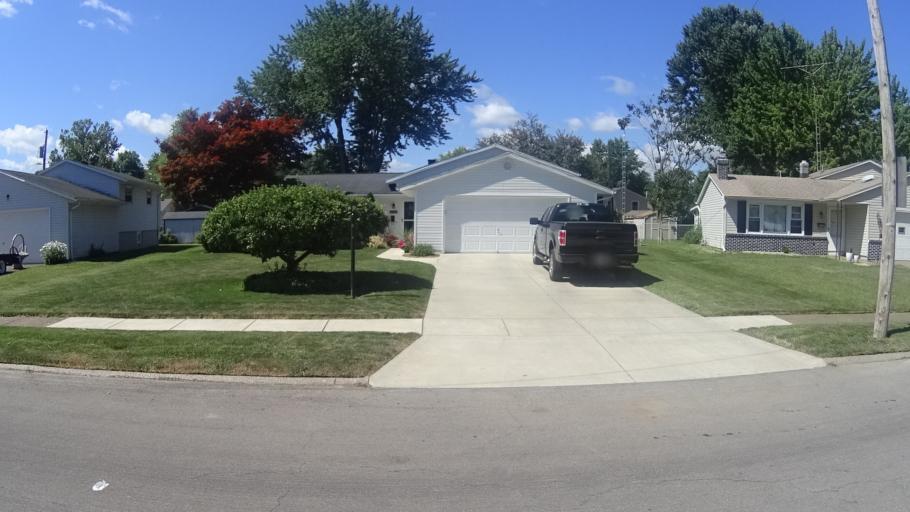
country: US
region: Ohio
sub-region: Erie County
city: Sandusky
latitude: 41.4252
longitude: -82.6529
